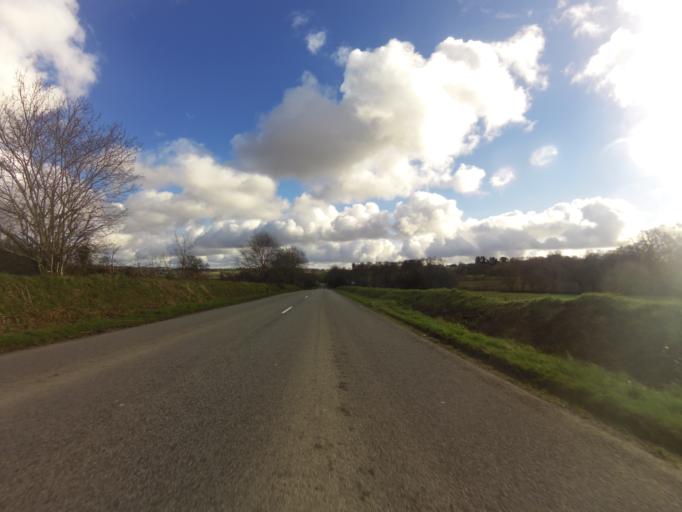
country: FR
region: Brittany
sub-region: Departement du Morbihan
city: Gourin
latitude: 48.1416
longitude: -3.5449
